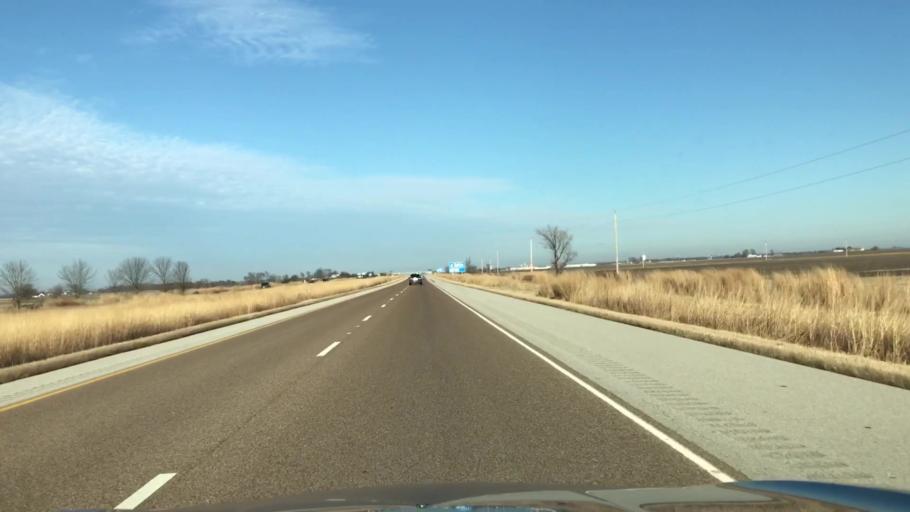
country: US
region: Illinois
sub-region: Montgomery County
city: Litchfield
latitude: 39.1404
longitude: -89.7054
